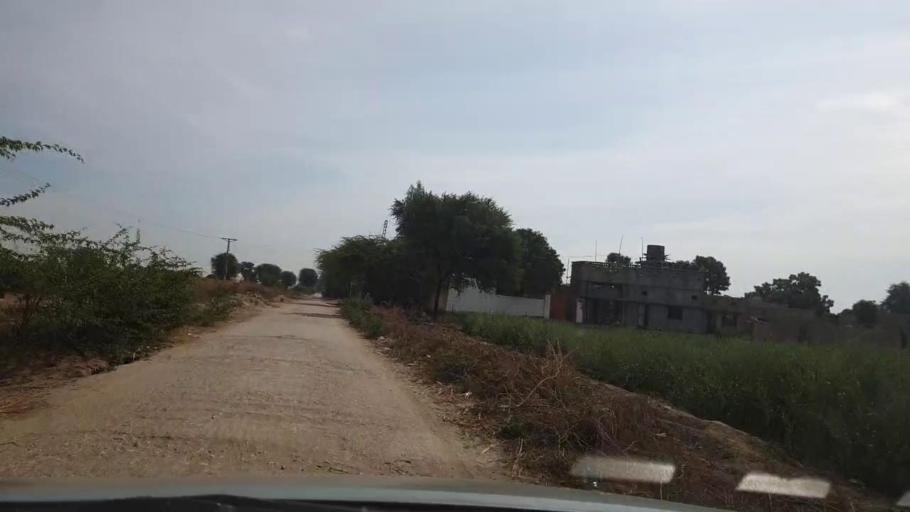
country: PK
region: Sindh
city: Kunri
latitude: 25.1611
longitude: 69.5848
